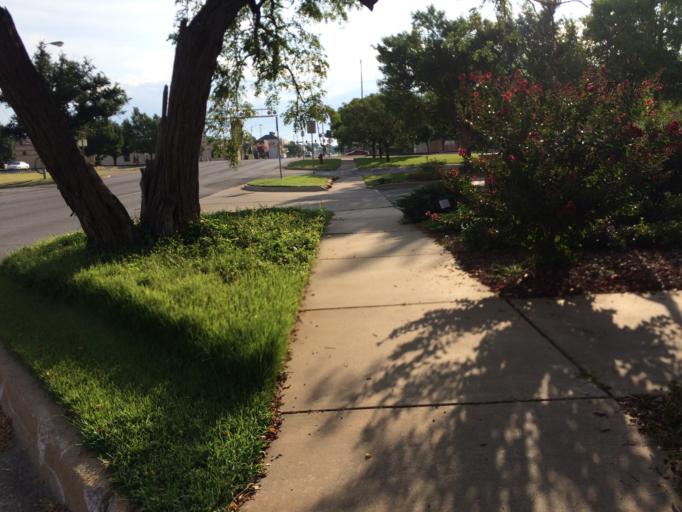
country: US
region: Oklahoma
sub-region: Cleveland County
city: Norman
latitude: 35.2213
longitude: -97.4449
